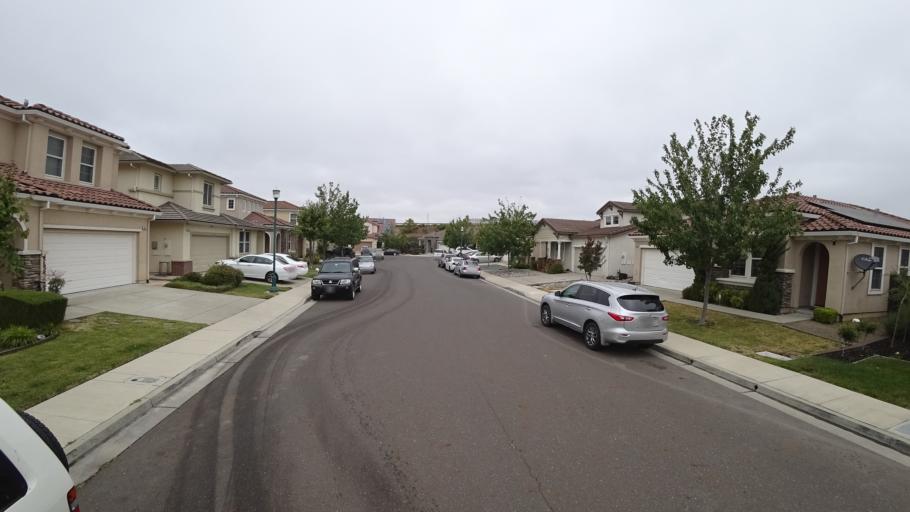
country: US
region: California
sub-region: Alameda County
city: Hayward
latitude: 37.6110
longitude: -122.0919
